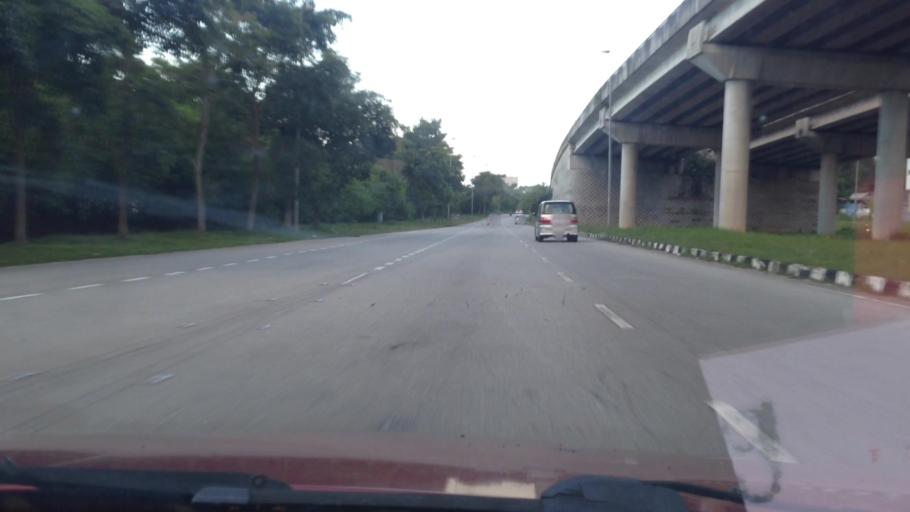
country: MY
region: Selangor
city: Shah Alam
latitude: 3.1007
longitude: 101.5477
